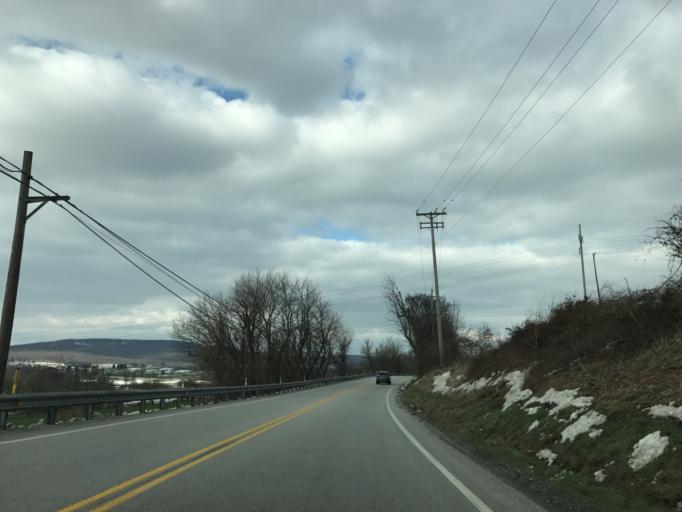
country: US
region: Pennsylvania
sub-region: York County
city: Parkville
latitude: 39.8132
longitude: -76.9445
